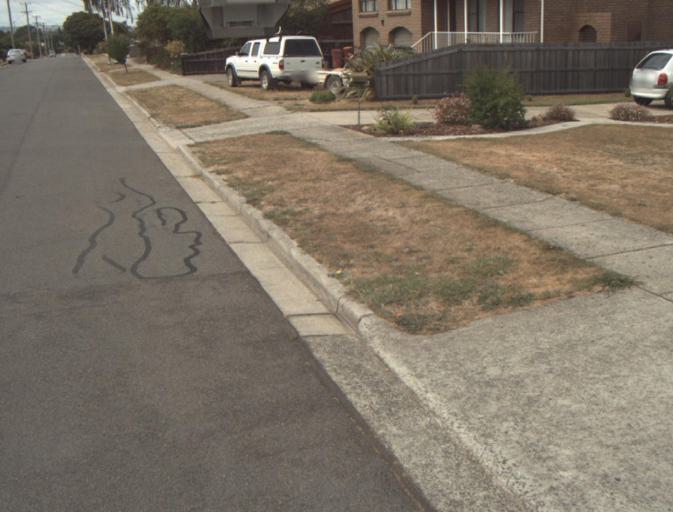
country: AU
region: Tasmania
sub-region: Launceston
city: Invermay
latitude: -41.3903
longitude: 147.1181
